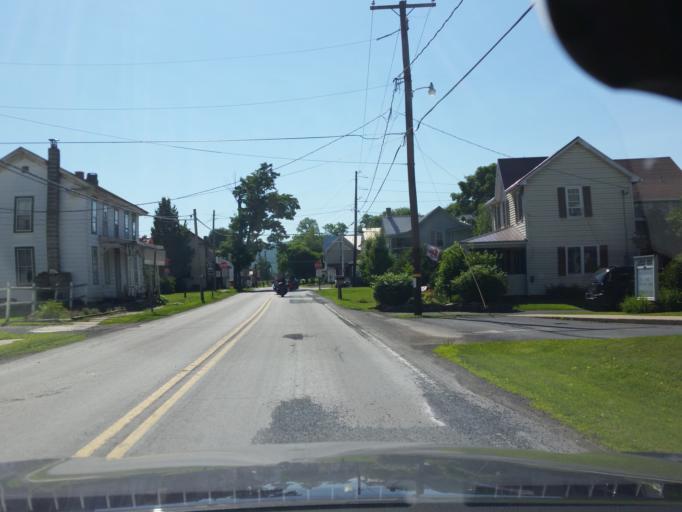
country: US
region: Pennsylvania
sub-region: Lycoming County
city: Duboistown
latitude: 41.1280
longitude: -77.0197
